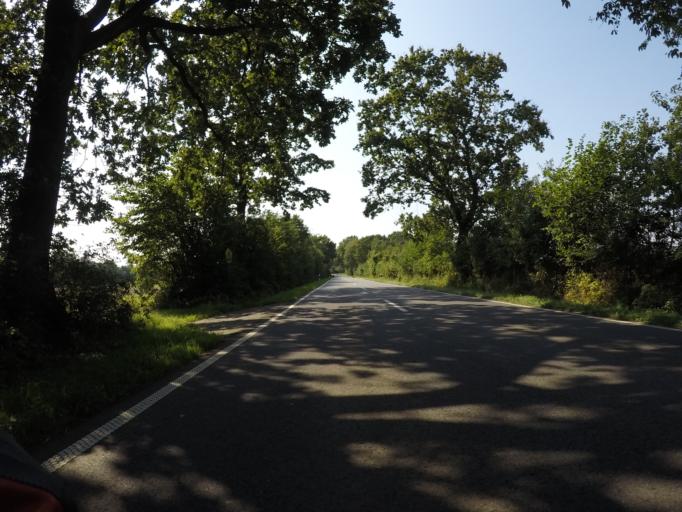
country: DE
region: Schleswig-Holstein
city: Huttblek
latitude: 53.8429
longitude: 10.0633
